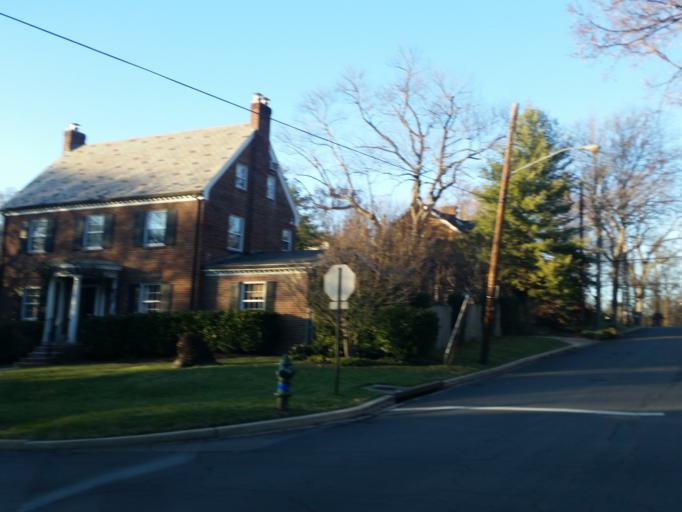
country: US
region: Maryland
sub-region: Montgomery County
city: Friendship Village
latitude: 38.9471
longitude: -77.0926
